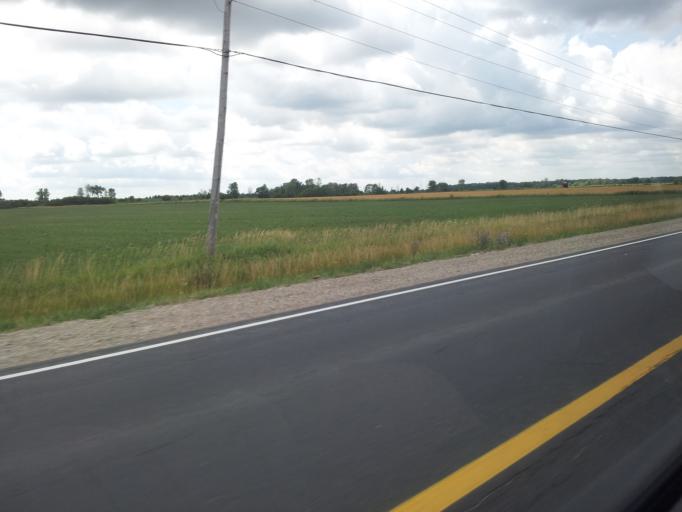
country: CA
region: Ontario
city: Stratford
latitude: 43.3699
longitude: -80.8706
